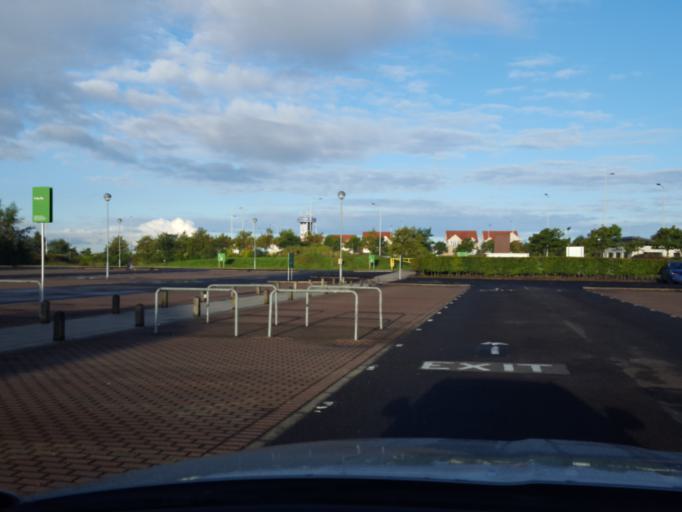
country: GB
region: Scotland
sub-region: Fife
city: Crossgates
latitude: 56.0762
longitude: -3.3957
